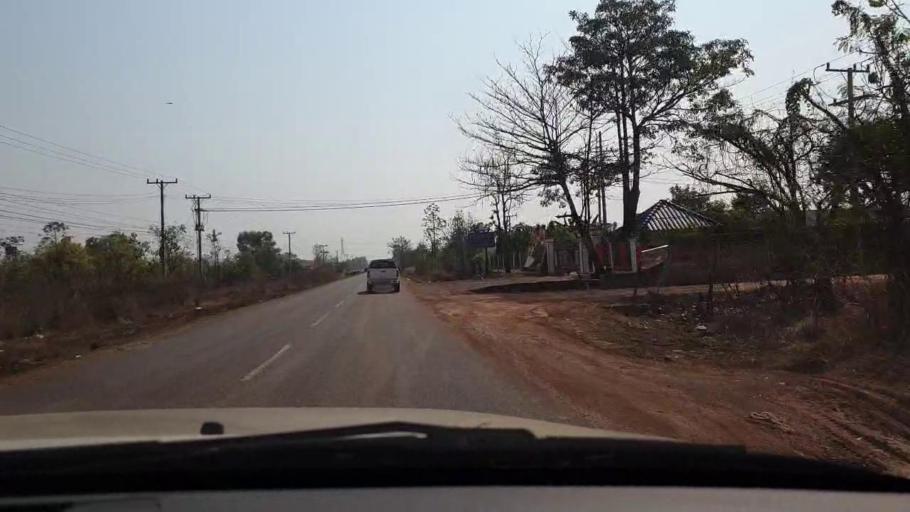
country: TH
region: Nong Khai
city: Nong Khai
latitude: 18.0521
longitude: 102.8495
